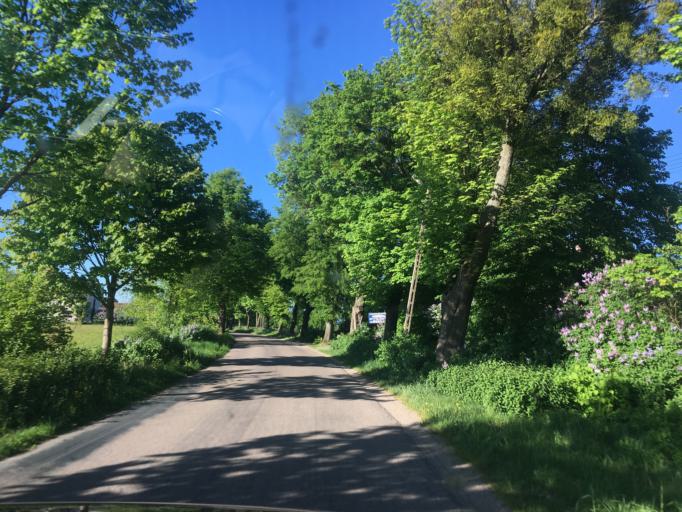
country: PL
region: Warmian-Masurian Voivodeship
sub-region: Powiat piski
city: Ruciane-Nida
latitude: 53.6760
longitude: 21.4927
